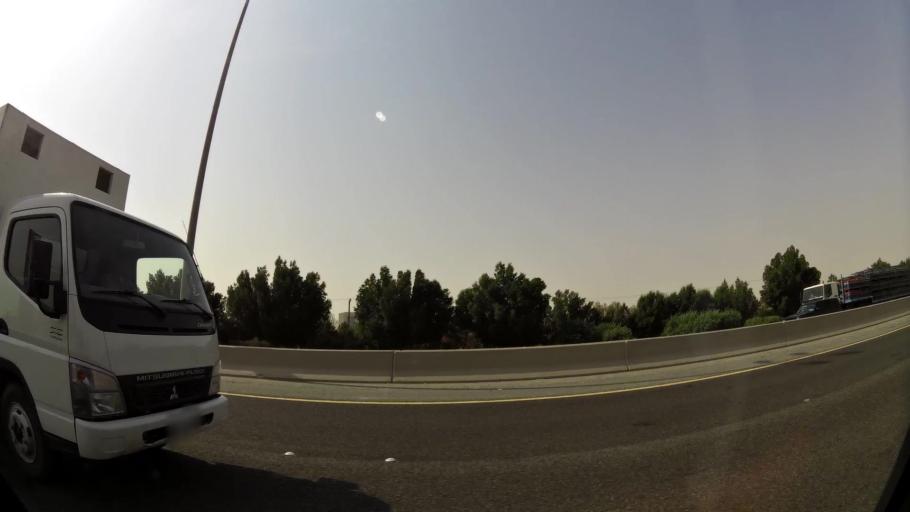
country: KW
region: Muhafazat al Jahra'
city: Al Jahra'
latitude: 29.3642
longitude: 47.6703
